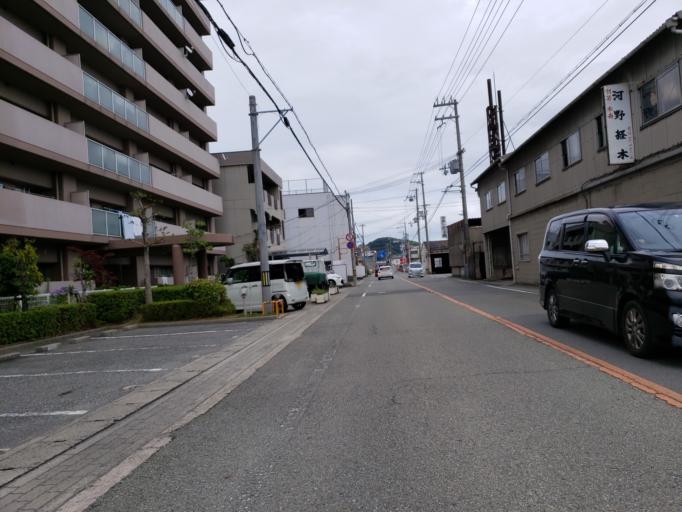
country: JP
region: Hyogo
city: Shirahamacho-usazakiminami
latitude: 34.7859
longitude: 134.7131
